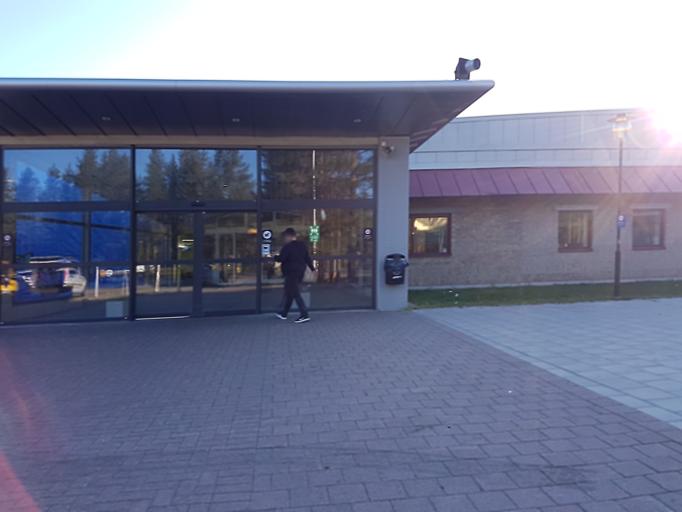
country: SE
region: Norrbotten
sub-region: Lulea Kommun
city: Bergnaset
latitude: 65.5492
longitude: 22.1243
